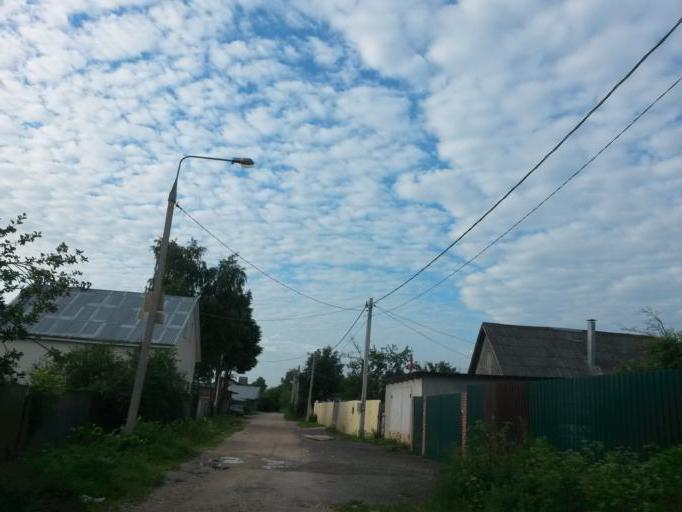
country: RU
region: Moskovskaya
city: Lyubuchany
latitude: 55.2548
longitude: 37.6122
